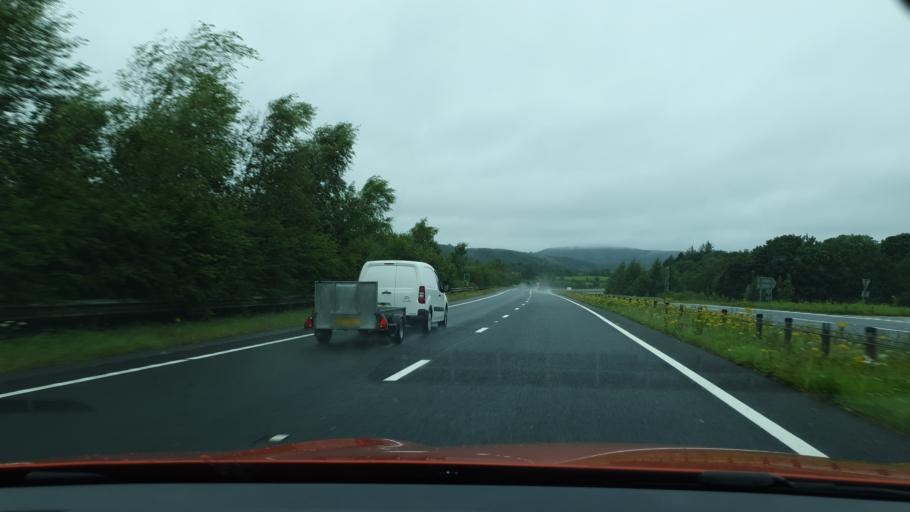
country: GB
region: England
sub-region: Cumbria
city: Grange-over-Sands
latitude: 54.2474
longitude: -2.9333
